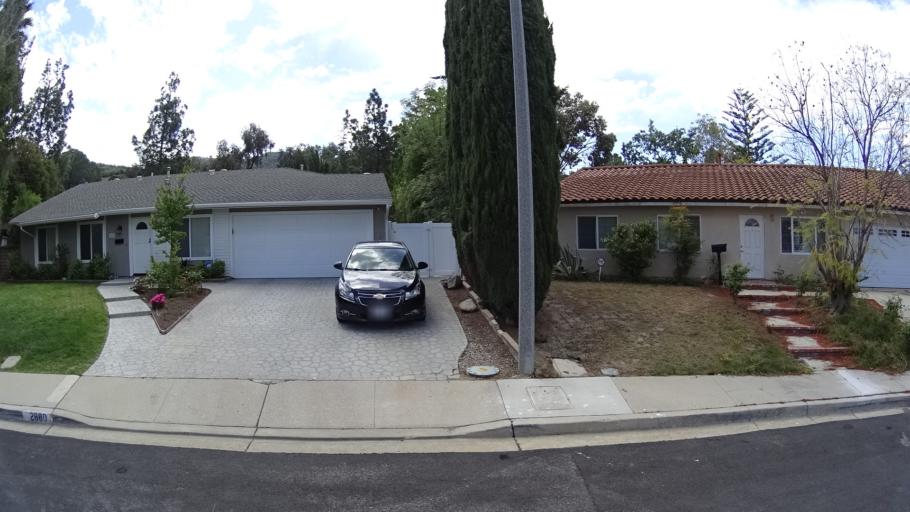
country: US
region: California
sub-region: Ventura County
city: Casa Conejo
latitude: 34.1649
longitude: -118.9383
